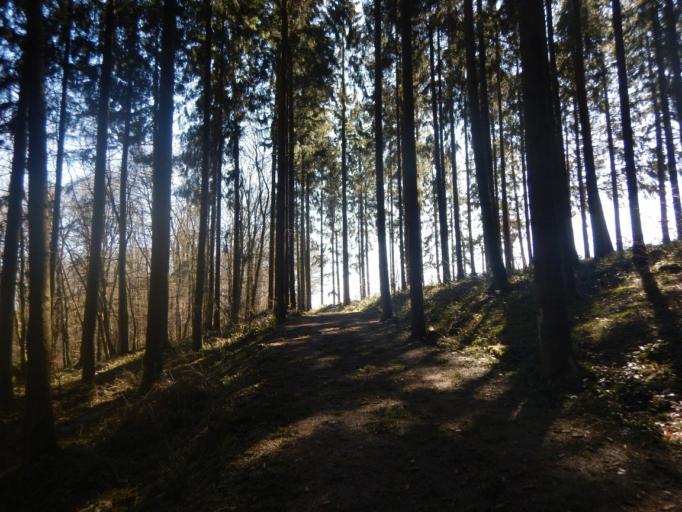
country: LU
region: Diekirch
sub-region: Canton de Wiltz
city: Eschweiler
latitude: 49.9976
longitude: 5.9251
